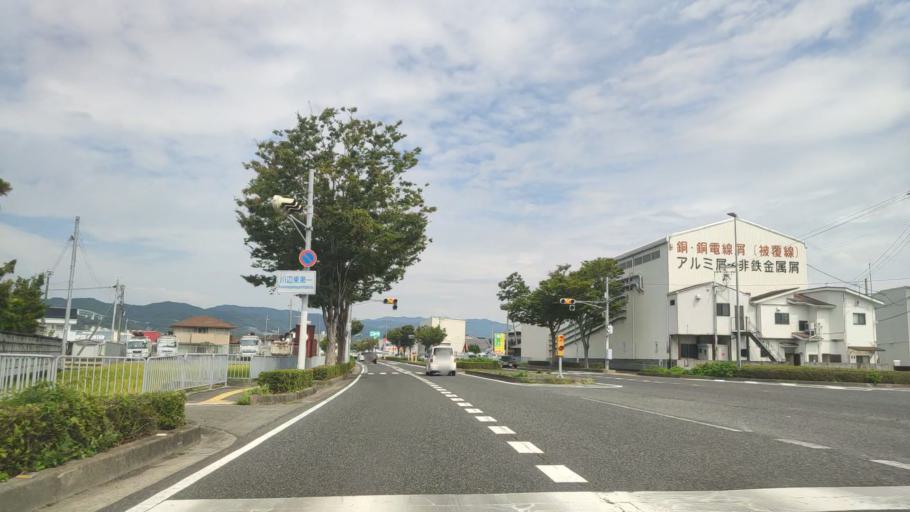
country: JP
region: Wakayama
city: Iwade
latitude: 34.2579
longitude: 135.2619
